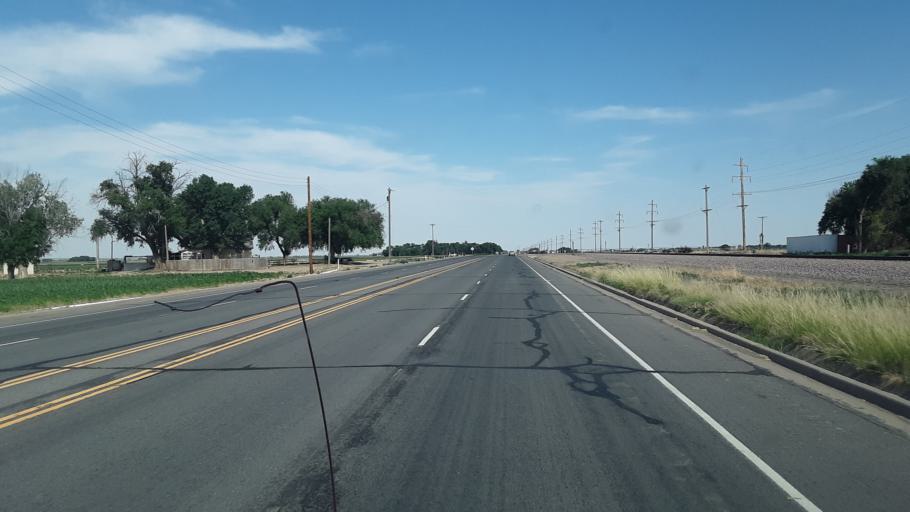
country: US
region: Colorado
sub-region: Otero County
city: Rocky Ford
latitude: 38.0945
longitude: -103.8231
